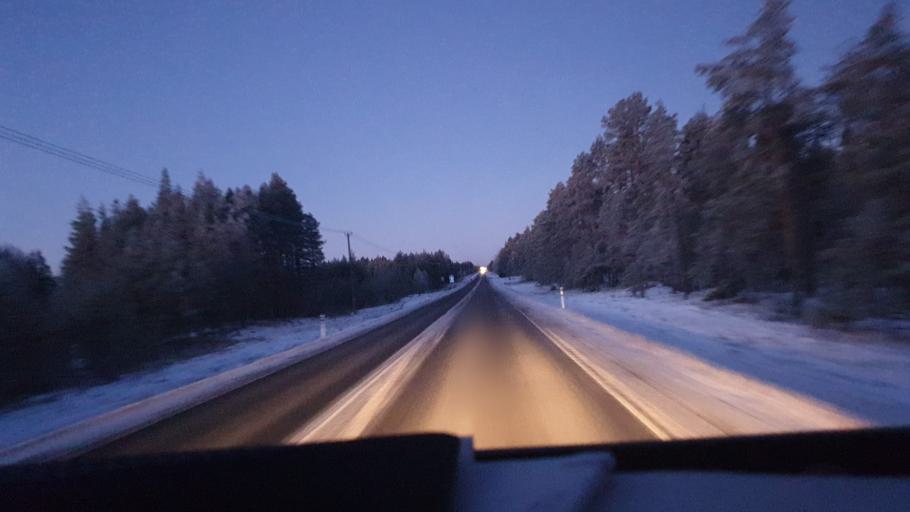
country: FI
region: Northern Ostrobothnia
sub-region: Raahe
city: Siikajoki
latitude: 64.6946
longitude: 24.6873
